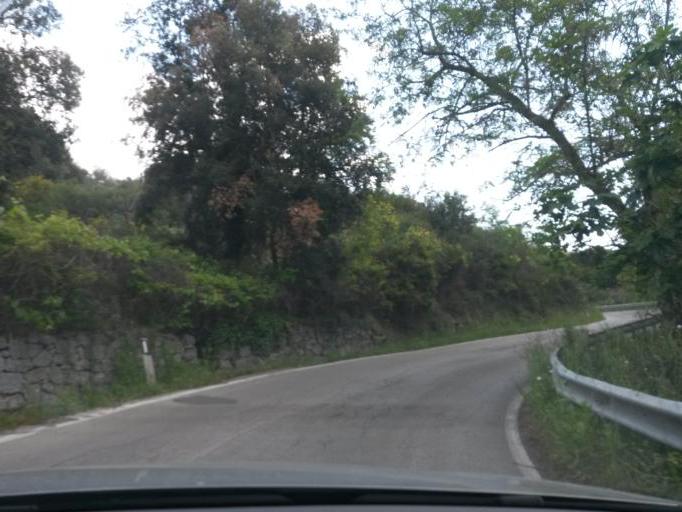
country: IT
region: Tuscany
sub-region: Provincia di Livorno
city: Campo nell'Elba
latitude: 42.7600
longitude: 10.2080
